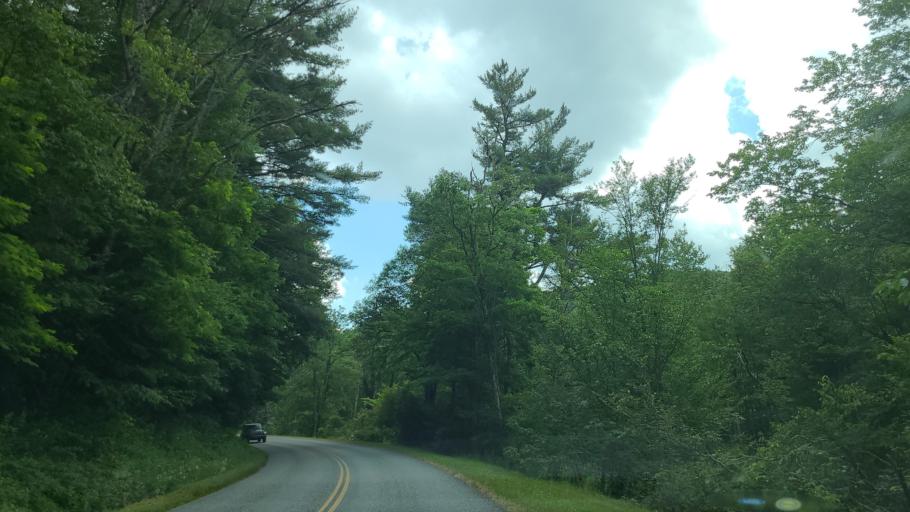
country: US
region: North Carolina
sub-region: Avery County
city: Newland
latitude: 35.9850
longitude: -81.8974
